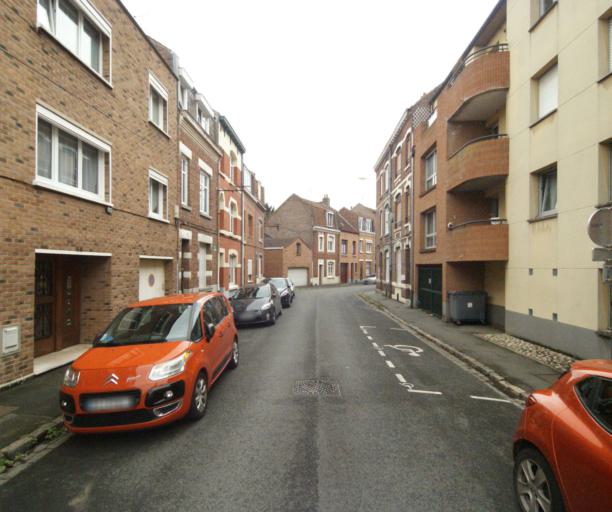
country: FR
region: Nord-Pas-de-Calais
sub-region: Departement du Nord
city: Ronchin
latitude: 50.6084
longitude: 3.0789
